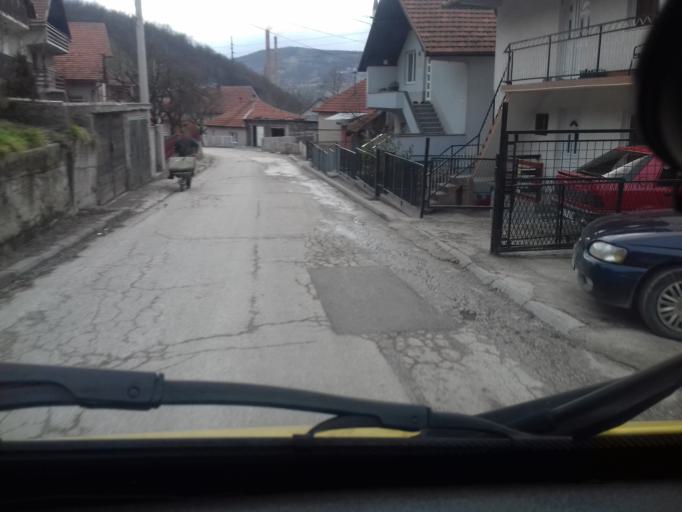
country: BA
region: Federation of Bosnia and Herzegovina
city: Zenica
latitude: 44.2346
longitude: 17.9110
